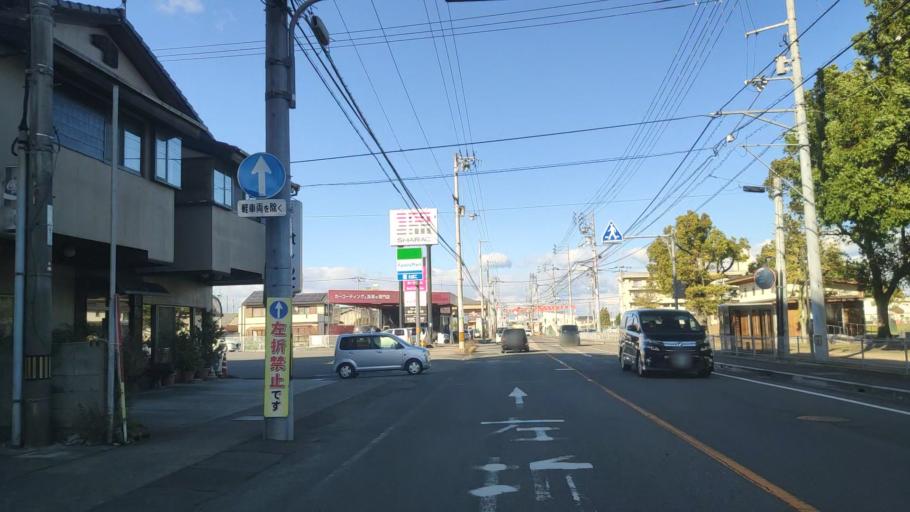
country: JP
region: Ehime
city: Saijo
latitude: 33.9171
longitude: 133.1919
